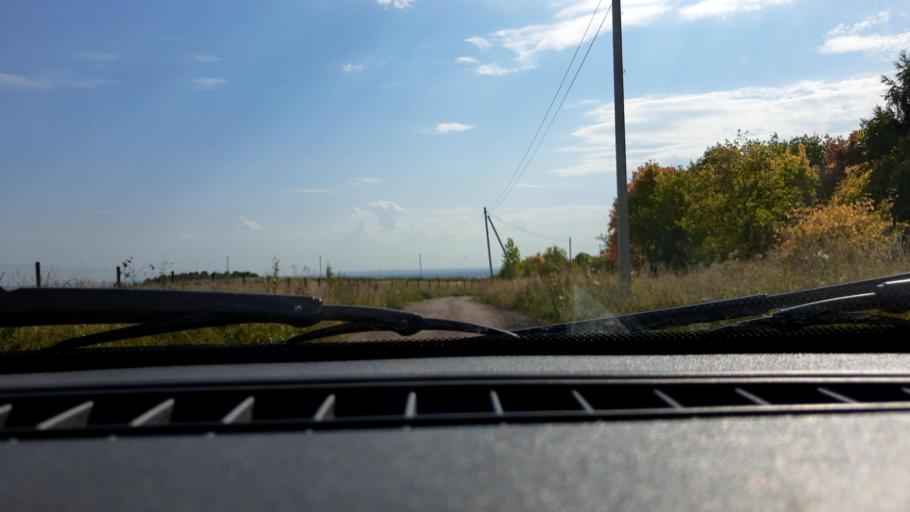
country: RU
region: Bashkortostan
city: Ufa
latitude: 54.8518
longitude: 56.1633
